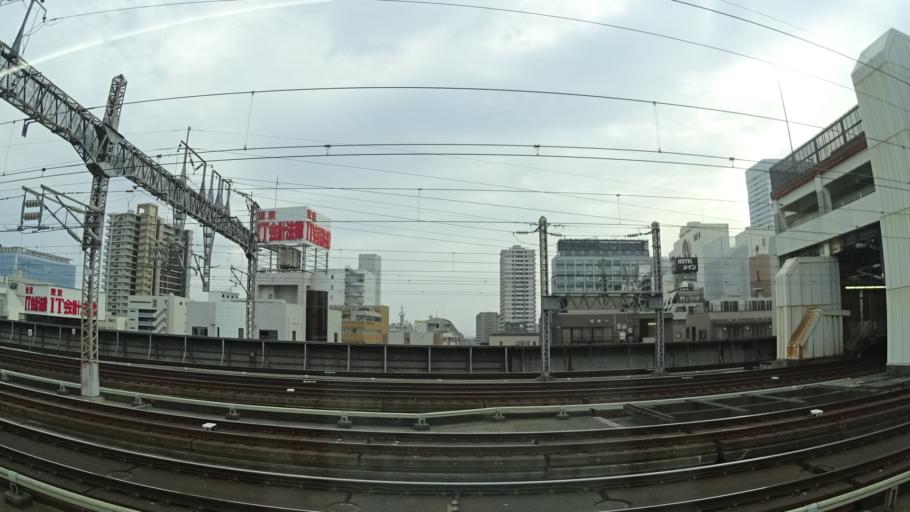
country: JP
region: Saitama
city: Yono
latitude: 35.9046
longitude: 139.6241
